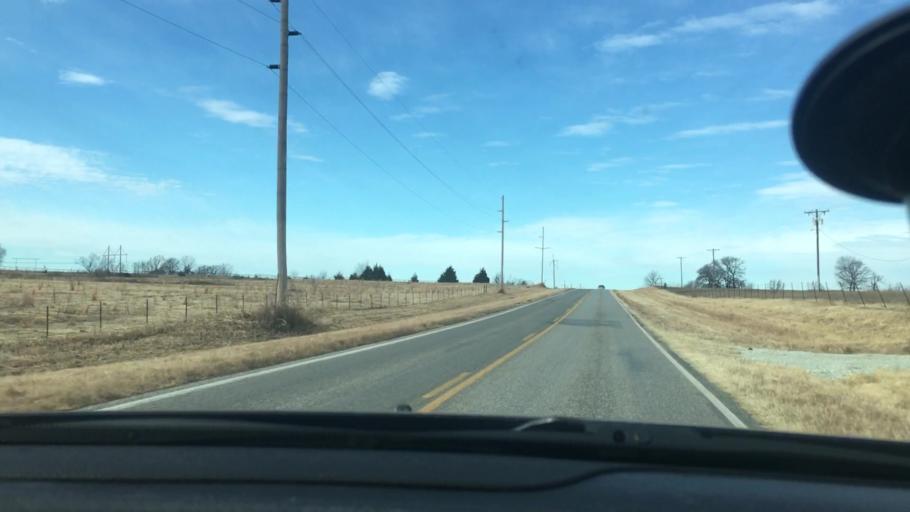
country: US
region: Oklahoma
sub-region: Seminole County
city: Konawa
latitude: 34.9418
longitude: -96.6911
